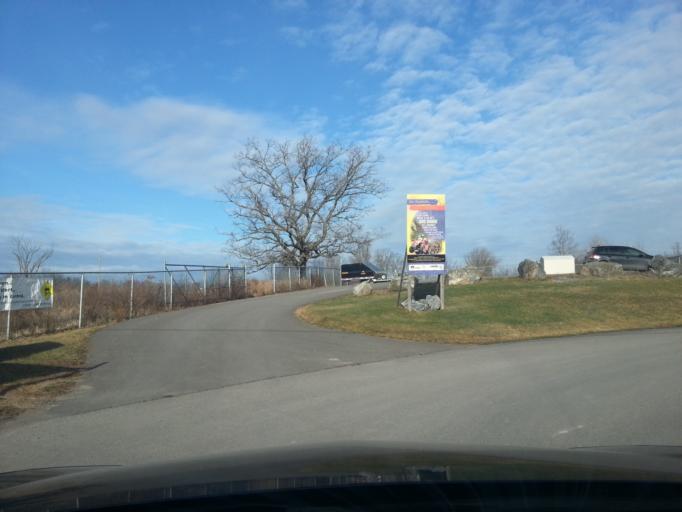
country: CA
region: Ontario
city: Quinte West
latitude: 44.5103
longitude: -77.4843
